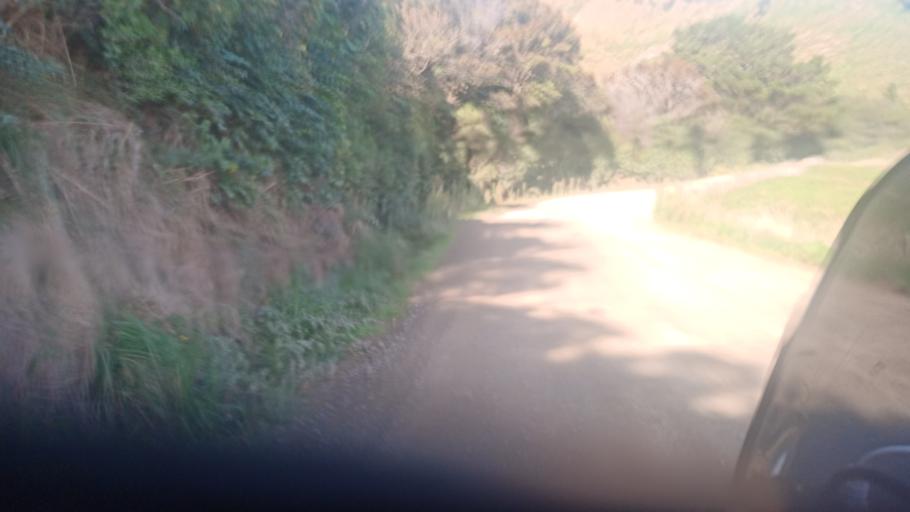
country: NZ
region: Gisborne
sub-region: Gisborne District
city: Gisborne
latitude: -38.4315
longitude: 177.5561
